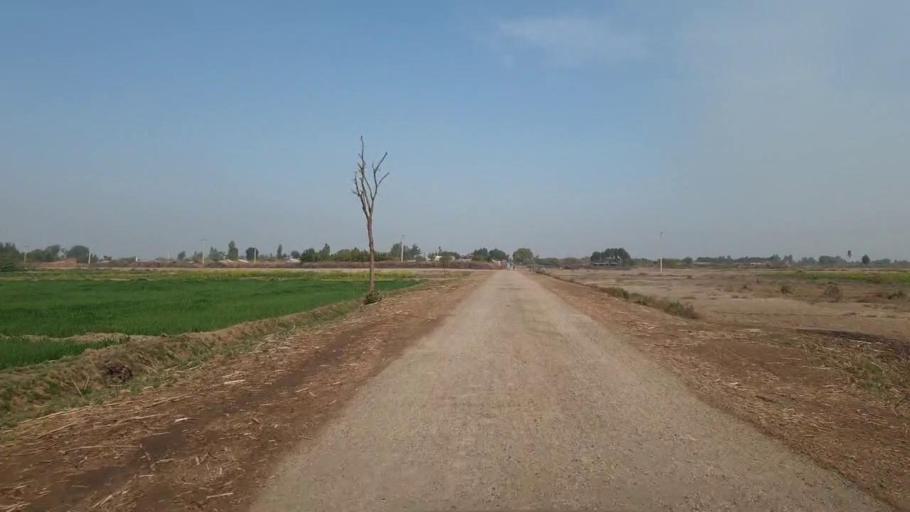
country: PK
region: Sindh
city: Mirwah Gorchani
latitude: 25.3747
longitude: 69.1606
